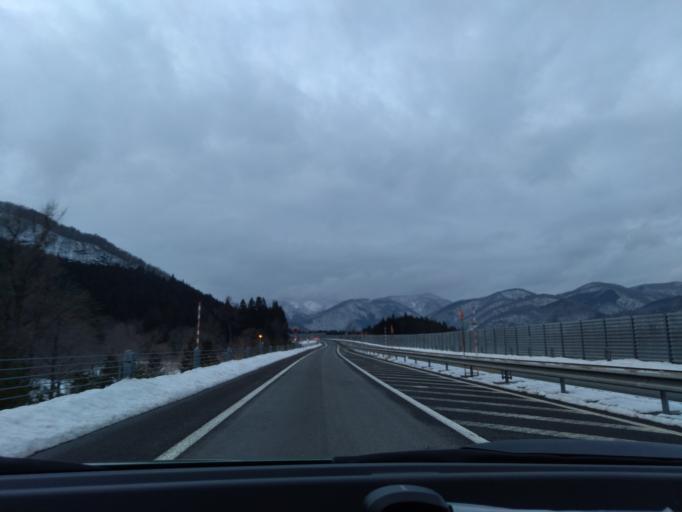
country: JP
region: Iwate
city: Kitakami
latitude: 39.2958
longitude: 140.9439
